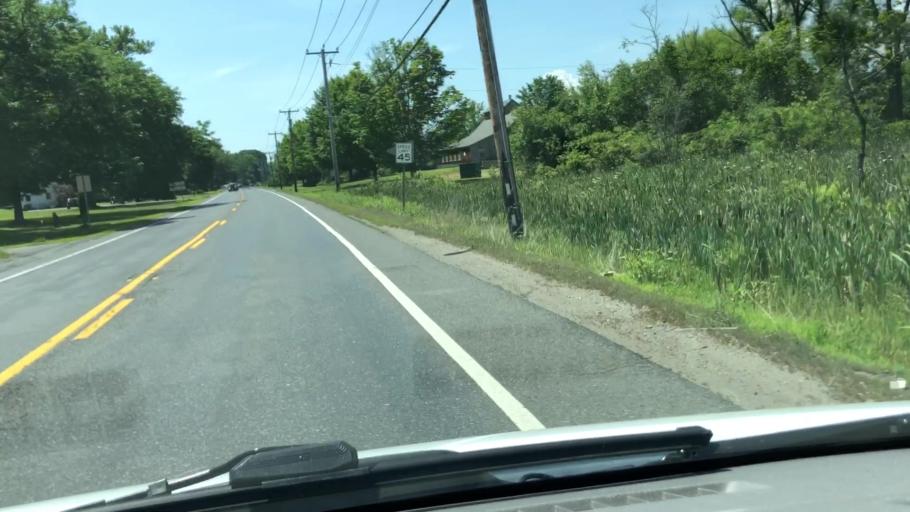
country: US
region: Massachusetts
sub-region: Franklin County
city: Greenfield
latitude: 42.5374
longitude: -72.6031
